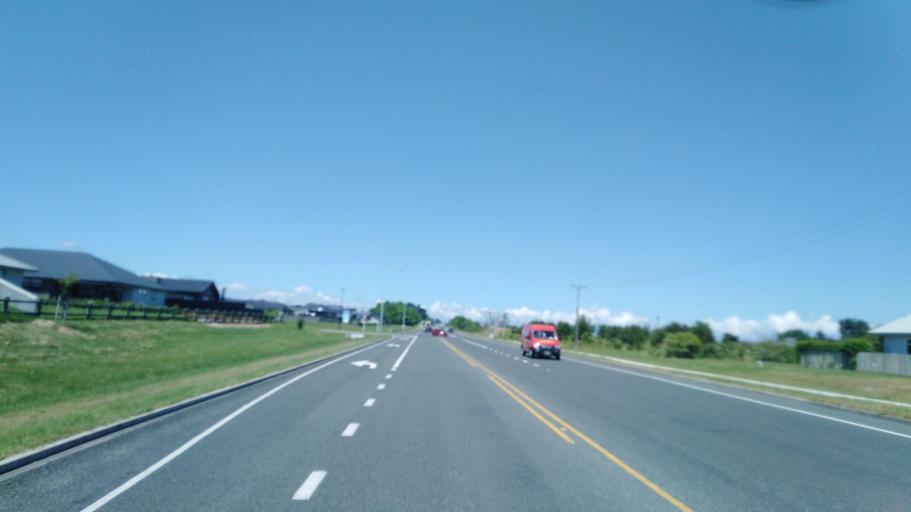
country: NZ
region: Waikato
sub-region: Taupo District
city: Taupo
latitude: -38.7252
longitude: 176.0762
